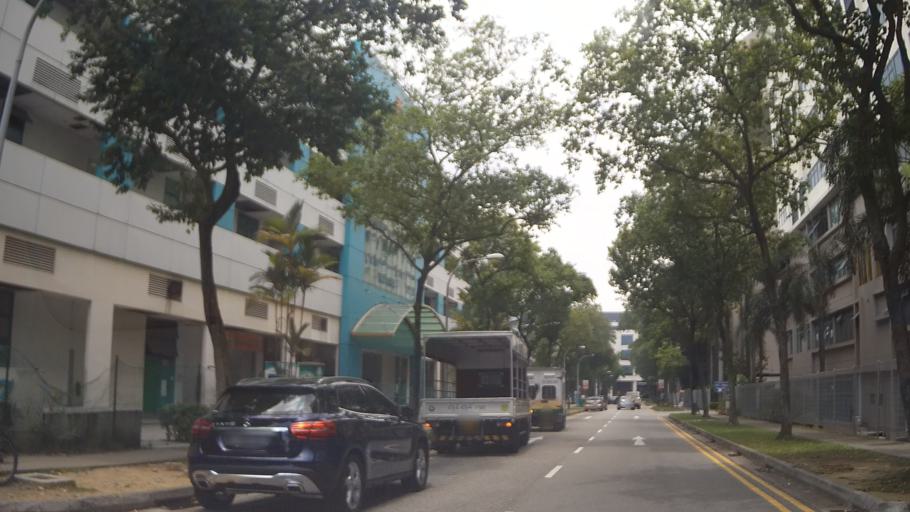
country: MY
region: Johor
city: Johor Bahru
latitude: 1.4547
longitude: 103.7977
